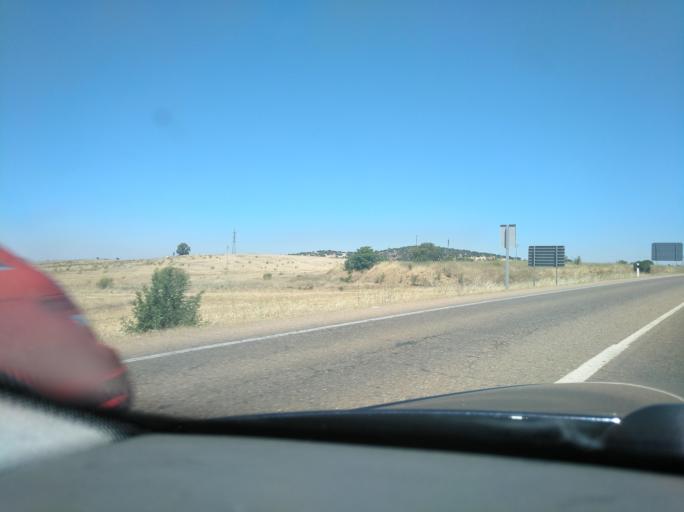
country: ES
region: Extremadura
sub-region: Provincia de Badajoz
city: Olivenza
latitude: 38.6969
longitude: -7.0902
